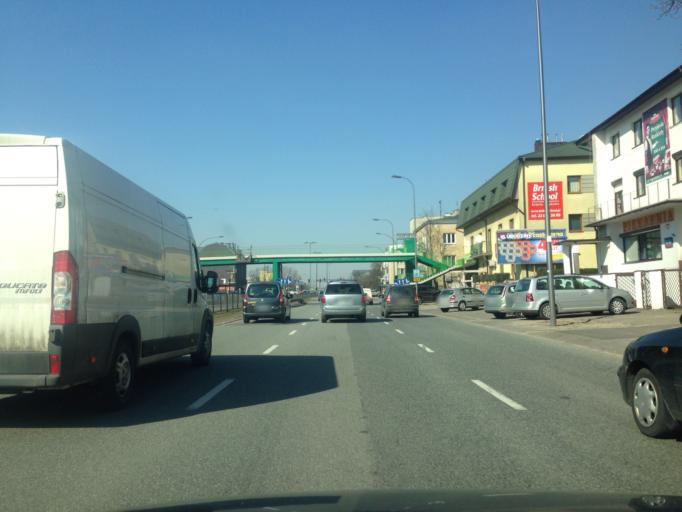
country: PL
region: Masovian Voivodeship
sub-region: Warszawa
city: Wilanow
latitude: 52.1849
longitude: 21.0661
